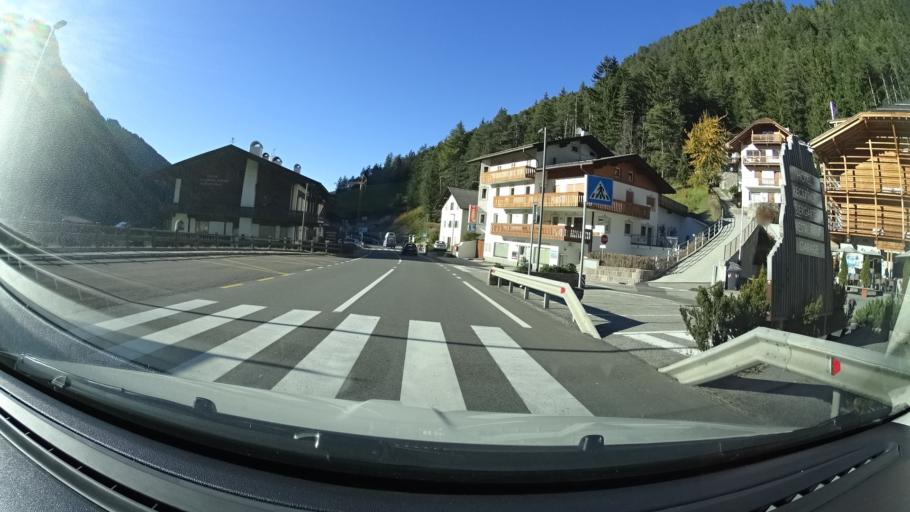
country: IT
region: Trentino-Alto Adige
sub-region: Bolzano
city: Santa Cristina Valgardena
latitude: 46.5605
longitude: 11.7079
